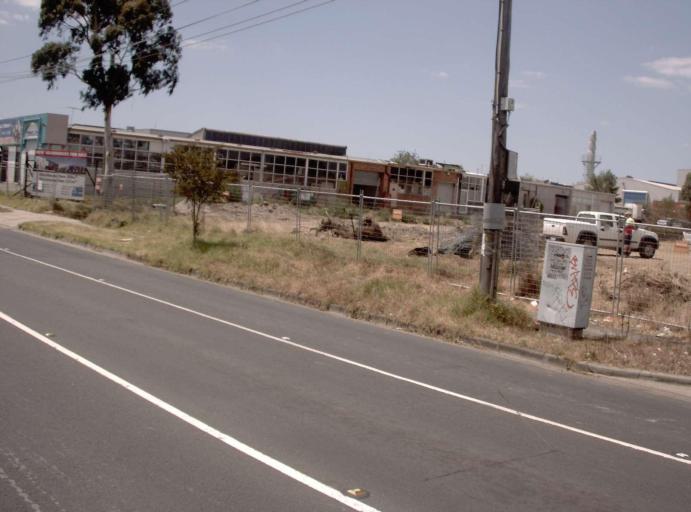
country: AU
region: Victoria
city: Highett
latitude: -37.9471
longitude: 145.0591
